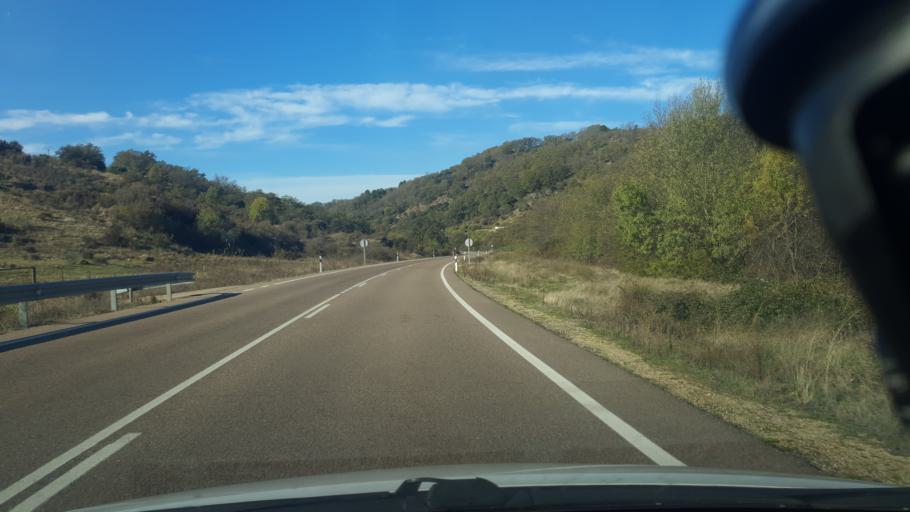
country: ES
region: Castille and Leon
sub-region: Provincia de Avila
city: Poyales del Hoyo
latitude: 40.1574
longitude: -5.1728
